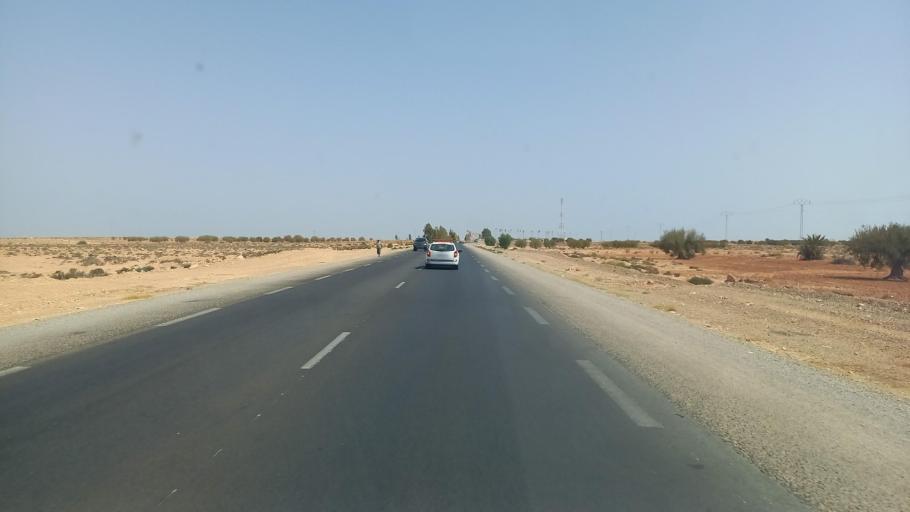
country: TN
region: Madanin
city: Medenine
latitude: 33.3810
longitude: 10.6990
